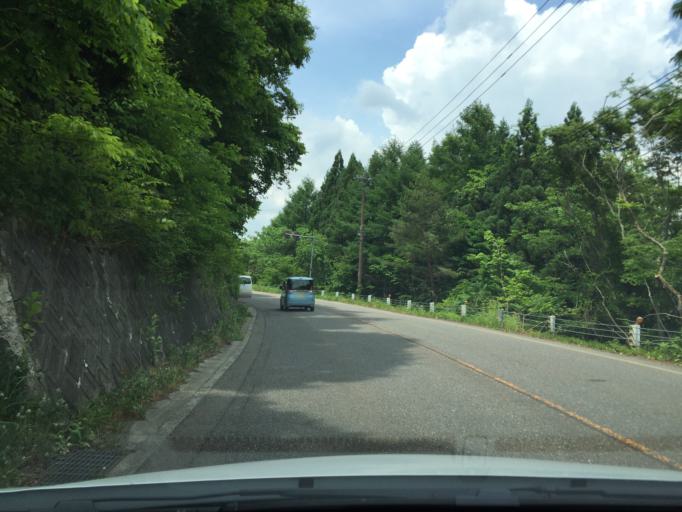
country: JP
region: Fukushima
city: Inawashiro
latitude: 37.6360
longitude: 140.1033
